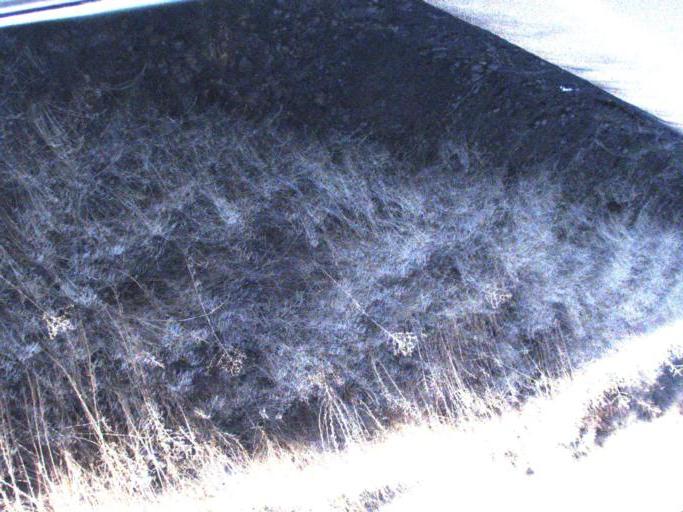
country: US
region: Washington
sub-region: Whitman County
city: Colfax
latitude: 46.7308
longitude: -117.4879
